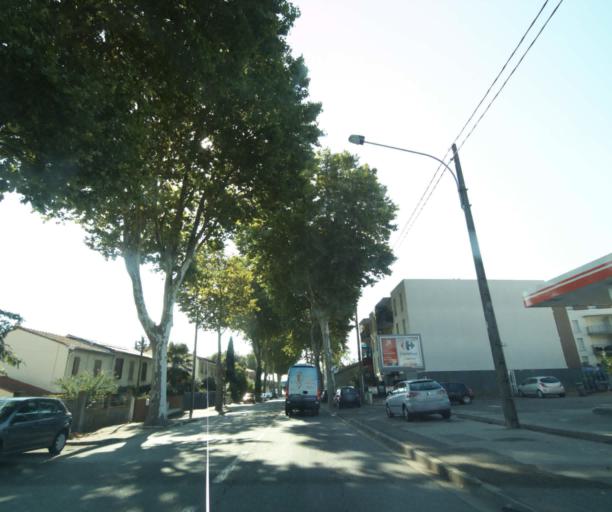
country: FR
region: Midi-Pyrenees
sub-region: Departement de la Haute-Garonne
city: Balma
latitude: 43.5947
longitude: 1.4889
